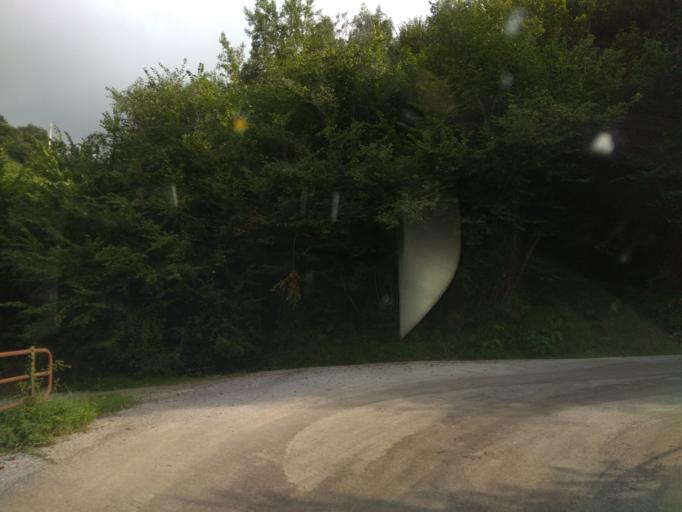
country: ES
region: Cantabria
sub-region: Provincia de Cantabria
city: San Vicente de la Barquera
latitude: 43.3177
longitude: -4.3903
